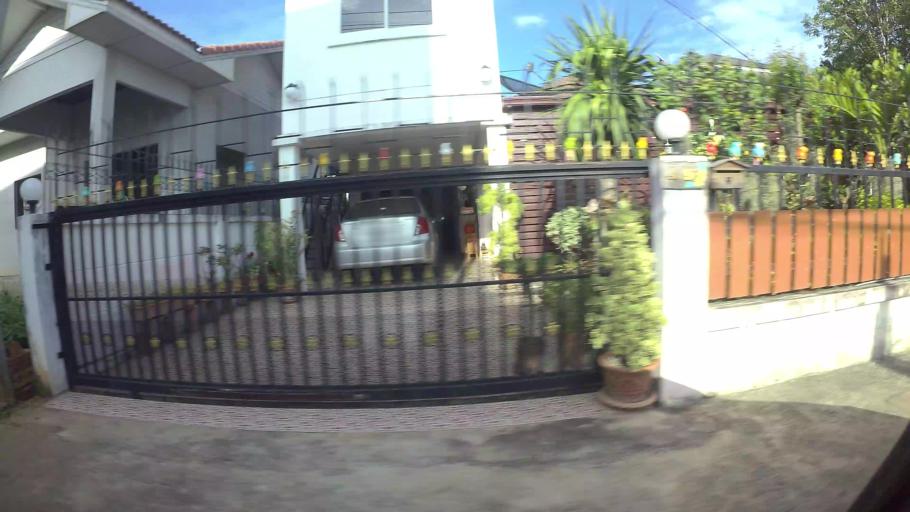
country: TH
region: Chon Buri
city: Sattahip
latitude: 12.6745
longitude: 100.9169
